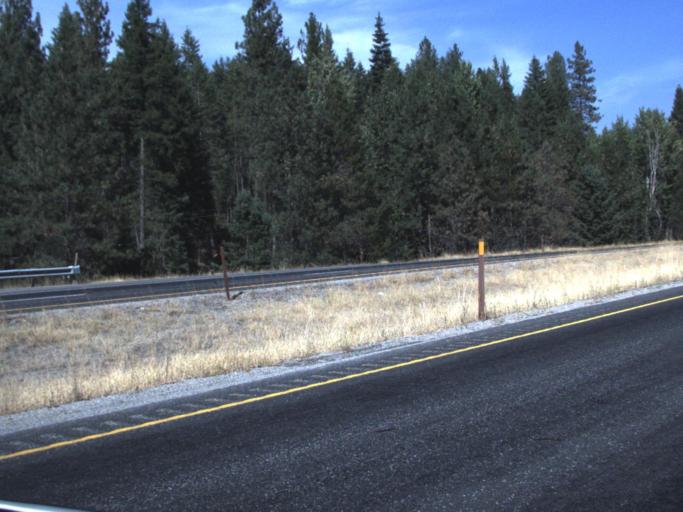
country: US
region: Washington
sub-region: Spokane County
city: Deer Park
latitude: 48.0775
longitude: -117.3279
